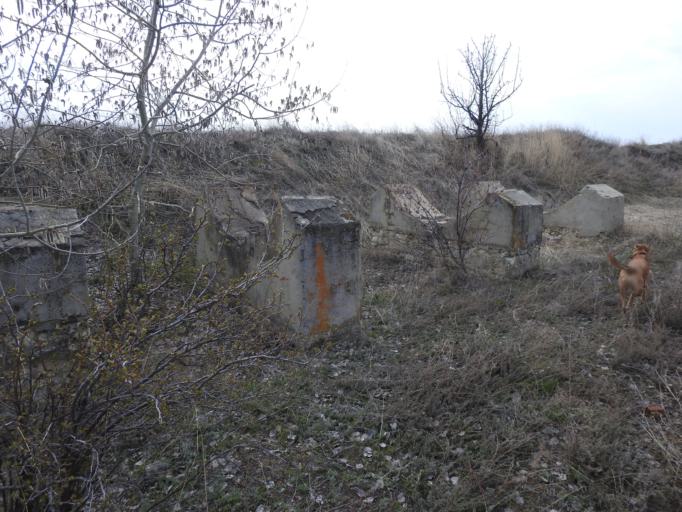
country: RU
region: Saratov
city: Voskresenskoye
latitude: 51.8107
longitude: 46.9247
